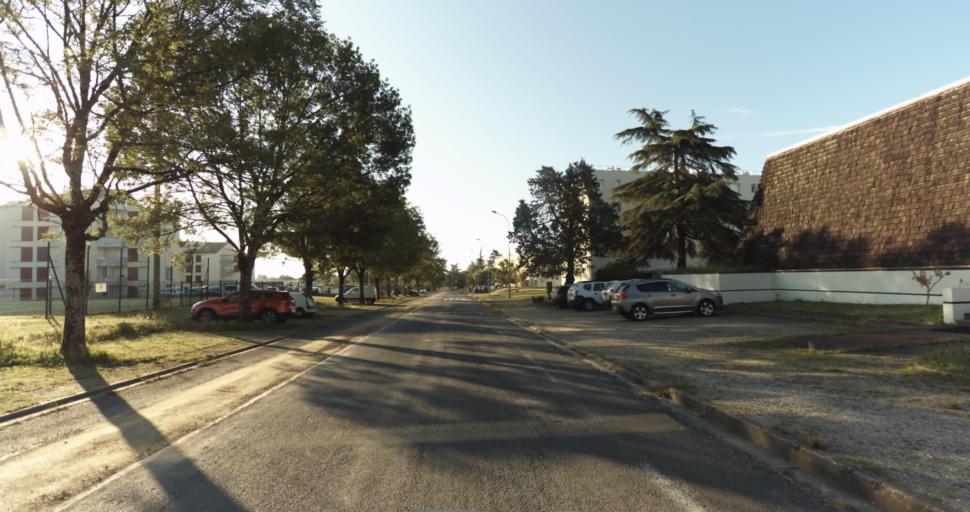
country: FR
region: Aquitaine
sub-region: Departement de la Gironde
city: Bazas
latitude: 44.4334
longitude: -0.2237
